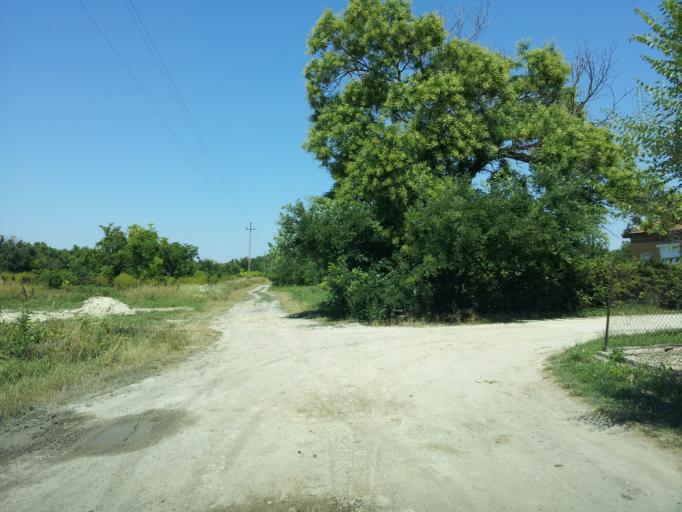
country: HU
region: Veszprem
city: Balatonkenese
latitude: 47.0442
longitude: 18.1790
